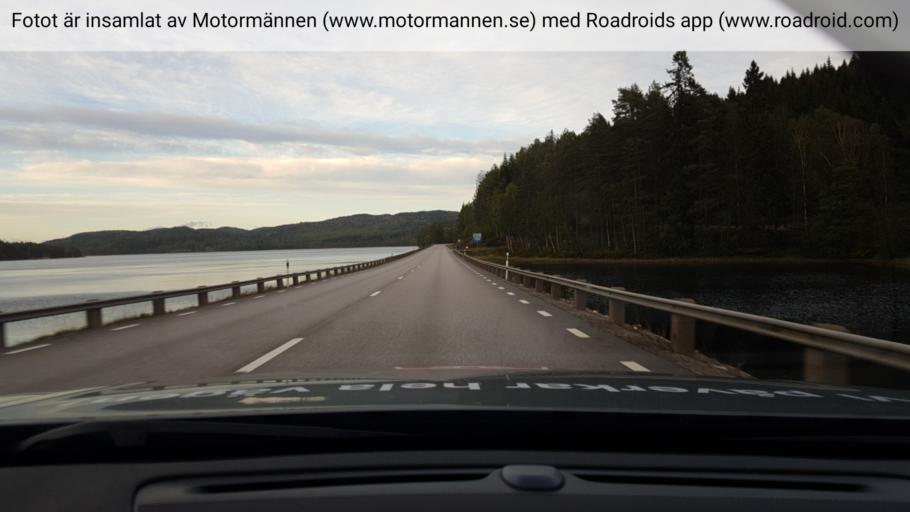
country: SE
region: Vaestra Goetaland
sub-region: Bengtsfors Kommun
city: Dals Langed
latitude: 59.0536
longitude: 12.4359
